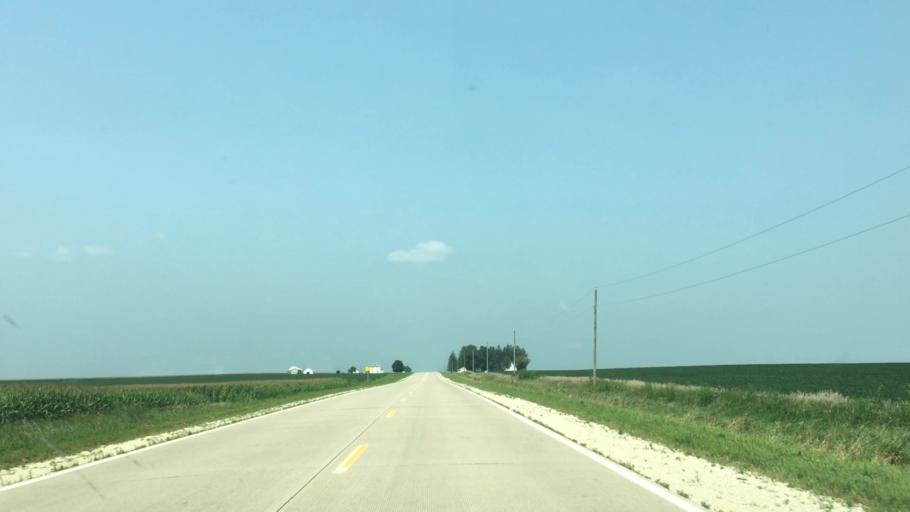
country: US
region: Iowa
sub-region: Fayette County
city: Oelwein
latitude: 42.7049
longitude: -91.8048
